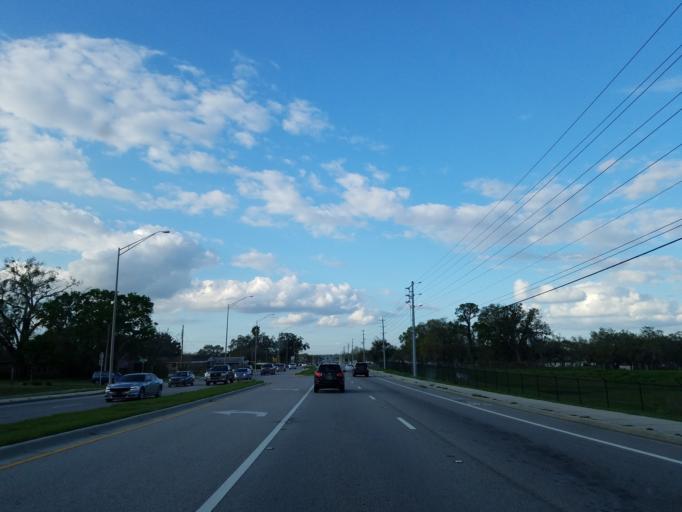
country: US
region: Florida
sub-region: Polk County
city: Lakeland Highlands
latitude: 27.9764
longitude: -81.9238
